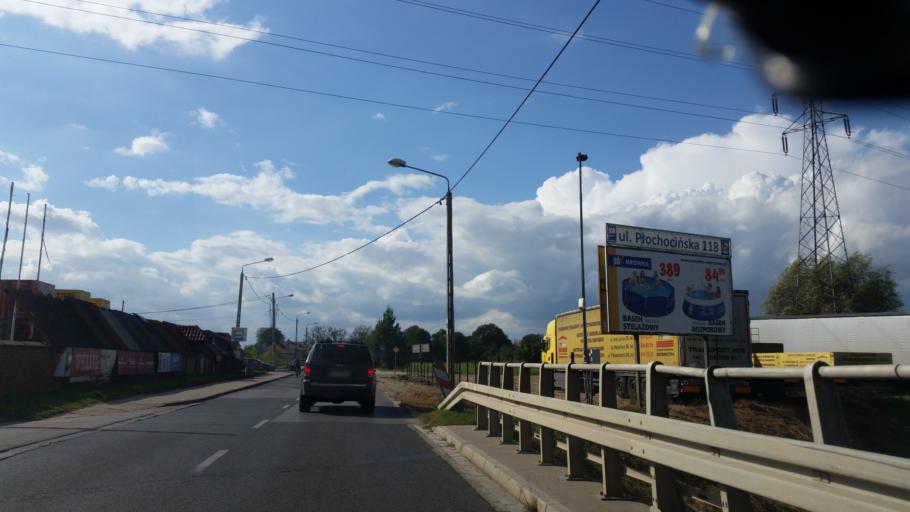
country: PL
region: Masovian Voivodeship
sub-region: Warszawa
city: Targowek
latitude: 52.3180
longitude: 21.0379
